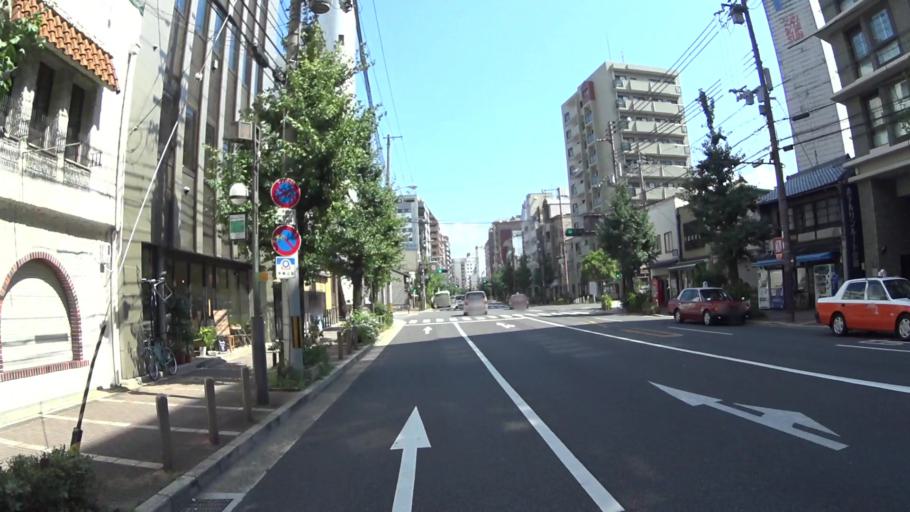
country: JP
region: Kyoto
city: Kyoto
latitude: 34.9980
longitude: 135.7674
